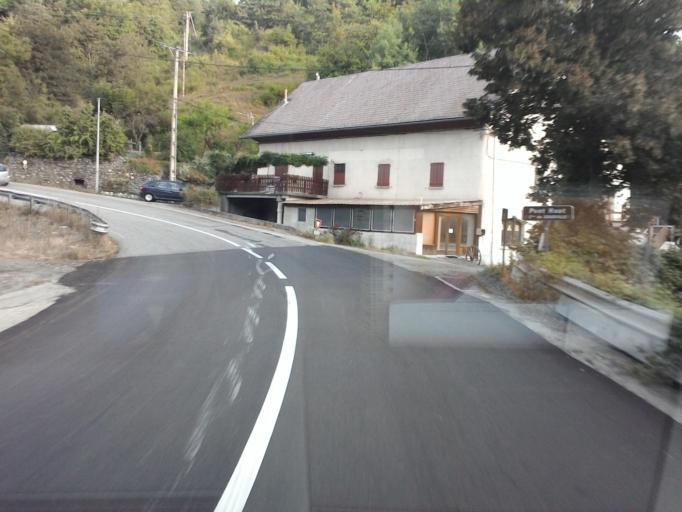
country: FR
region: Rhone-Alpes
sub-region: Departement de l'Isere
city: La Mure
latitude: 44.9021
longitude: 5.8169
